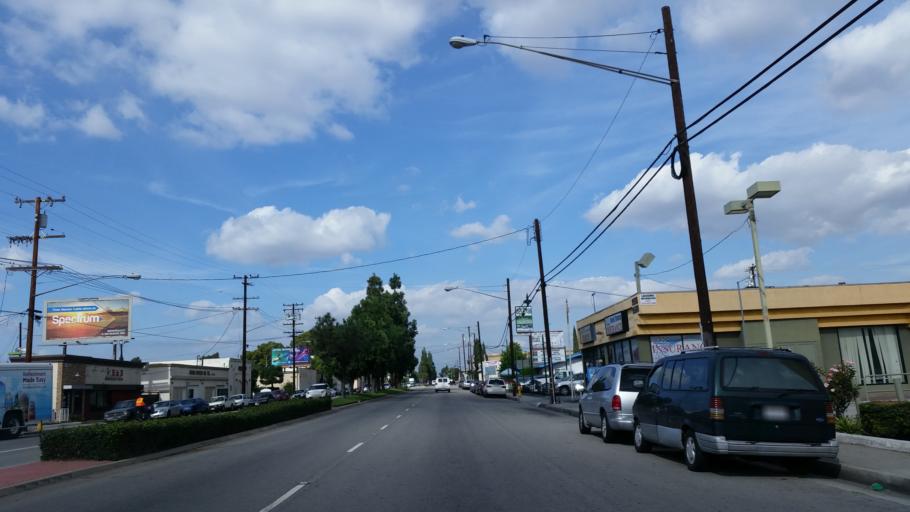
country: US
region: California
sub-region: Los Angeles County
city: Paramount
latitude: 33.8924
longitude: -118.1426
